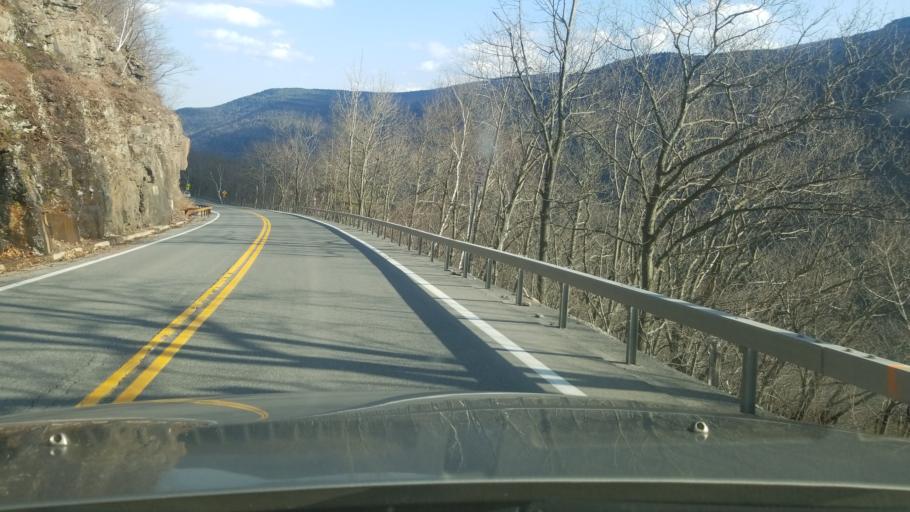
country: US
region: New York
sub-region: Greene County
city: Palenville
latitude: 42.1919
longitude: -74.0778
